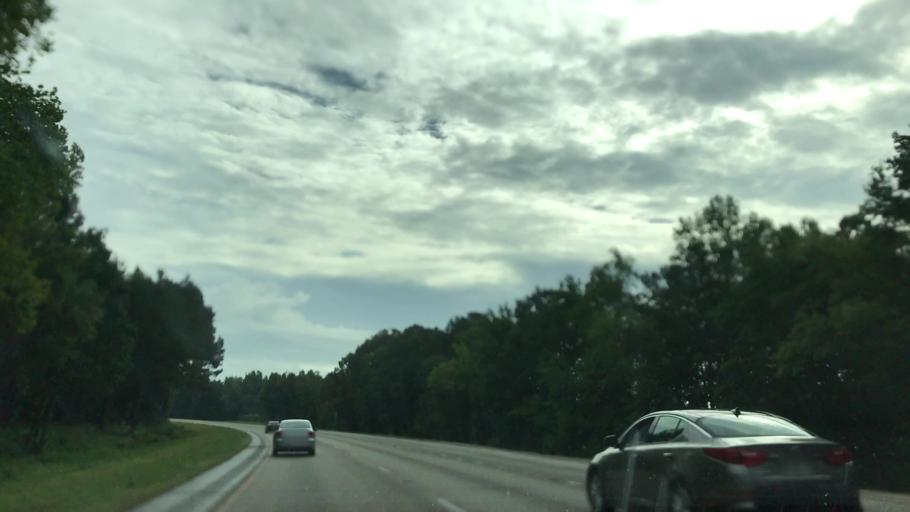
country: US
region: North Carolina
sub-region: Nash County
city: Red Oak
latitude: 36.0300
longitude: -77.8411
